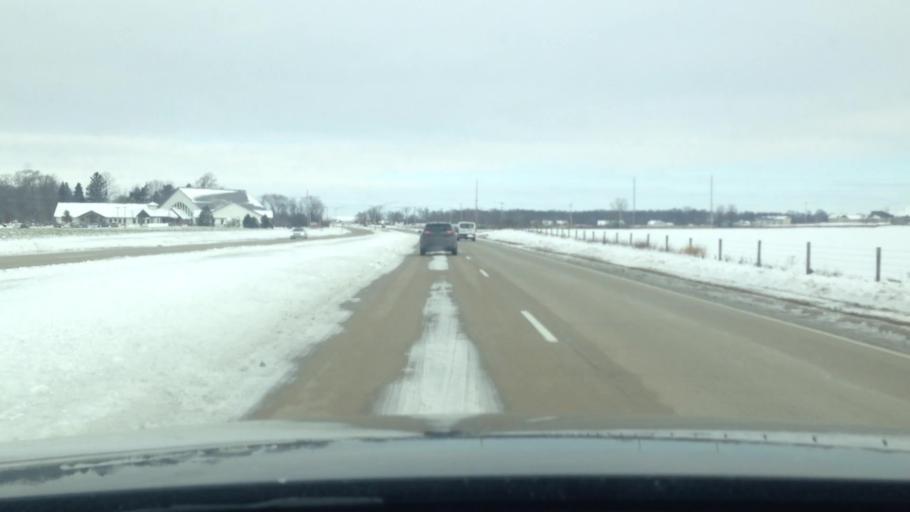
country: US
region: Wisconsin
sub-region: Walworth County
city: Lake Geneva
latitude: 42.5711
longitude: -88.4125
